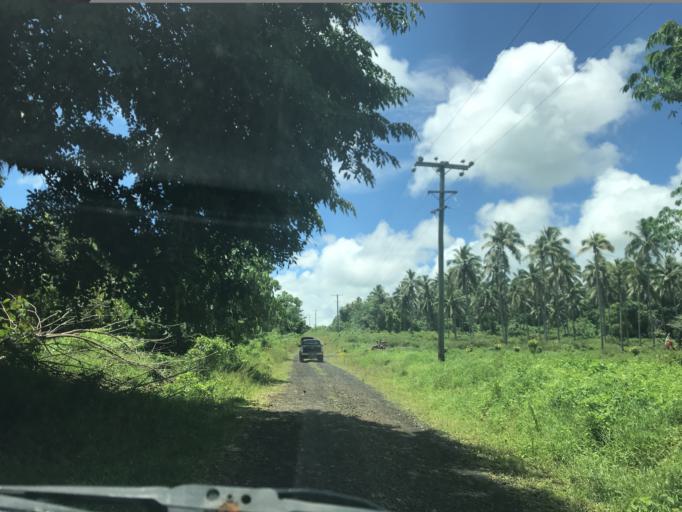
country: WS
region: Gagaifomauga
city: Safotu
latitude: -13.5465
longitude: -172.3056
